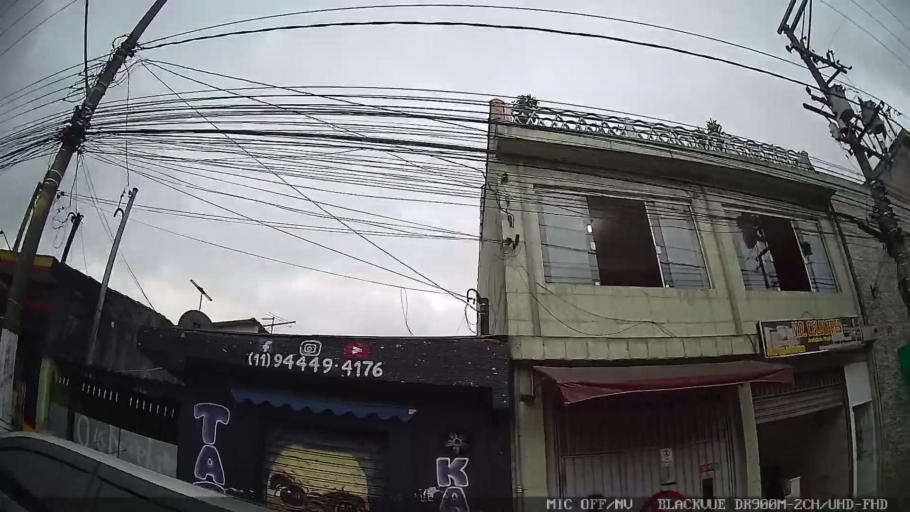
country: BR
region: Sao Paulo
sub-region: Itaquaquecetuba
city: Itaquaquecetuba
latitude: -23.4840
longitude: -46.3842
